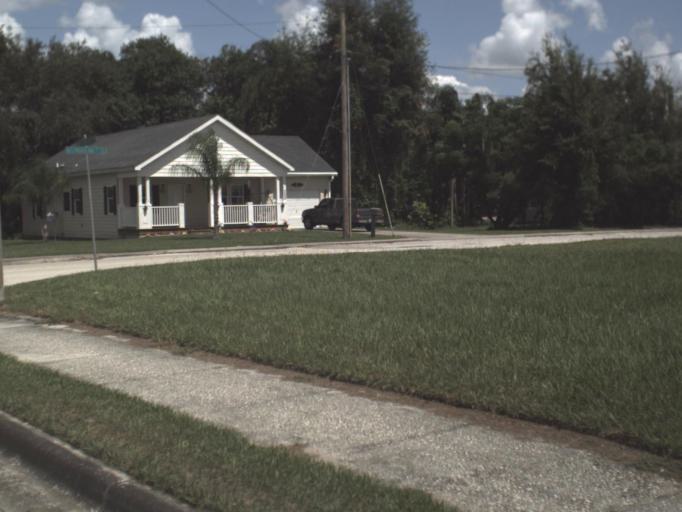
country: US
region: Florida
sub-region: Polk County
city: Bartow
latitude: 27.8903
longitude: -81.8281
